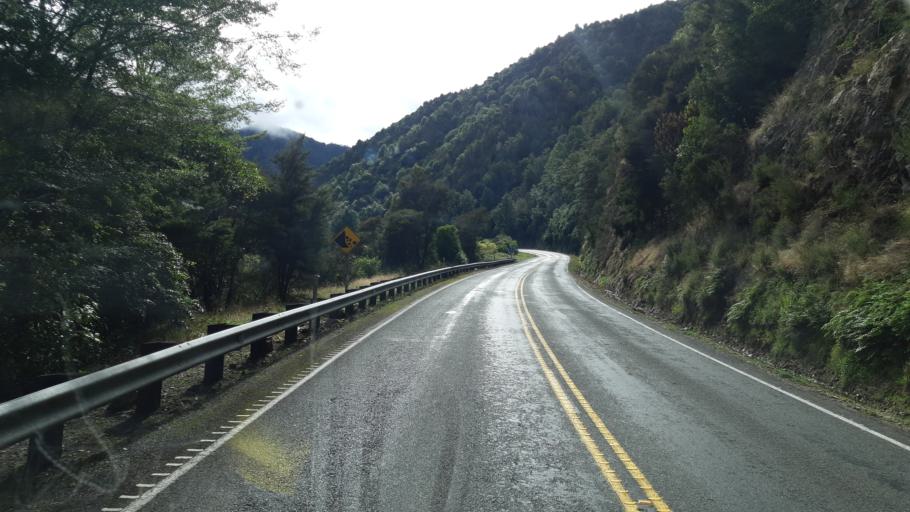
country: NZ
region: West Coast
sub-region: Buller District
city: Westport
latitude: -41.7748
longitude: 172.2238
